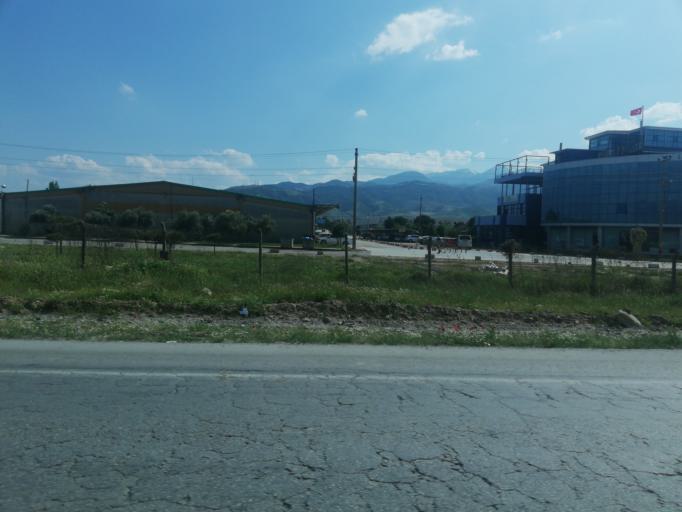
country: TR
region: Manisa
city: Alasehir
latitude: 38.3583
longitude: 28.5454
